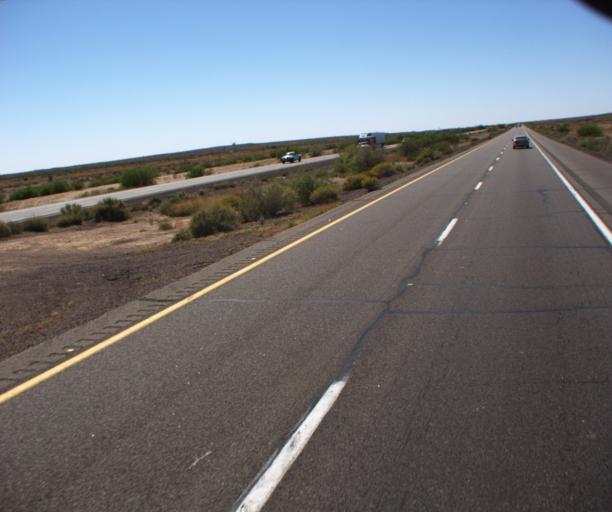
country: US
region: Arizona
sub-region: Maricopa County
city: Gila Bend
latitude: 32.8833
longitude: -113.0943
